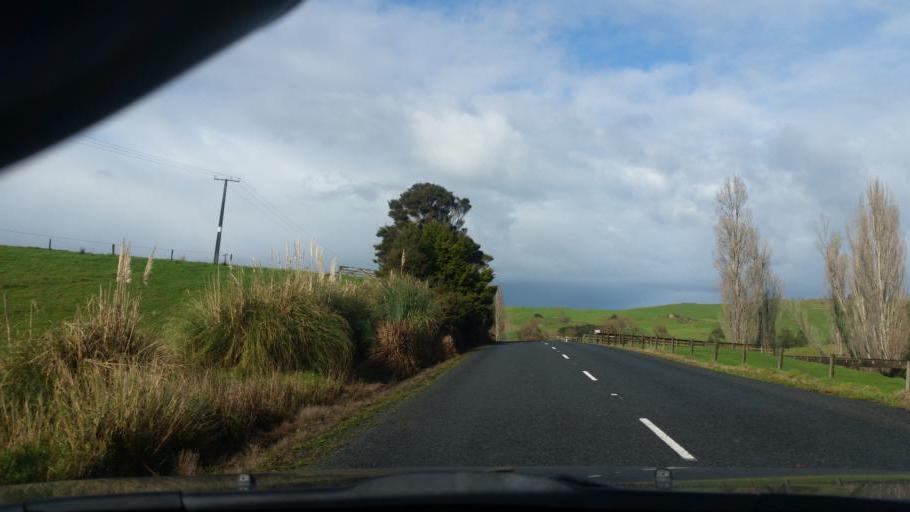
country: NZ
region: Northland
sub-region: Kaipara District
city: Dargaville
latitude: -35.8186
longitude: 173.9252
